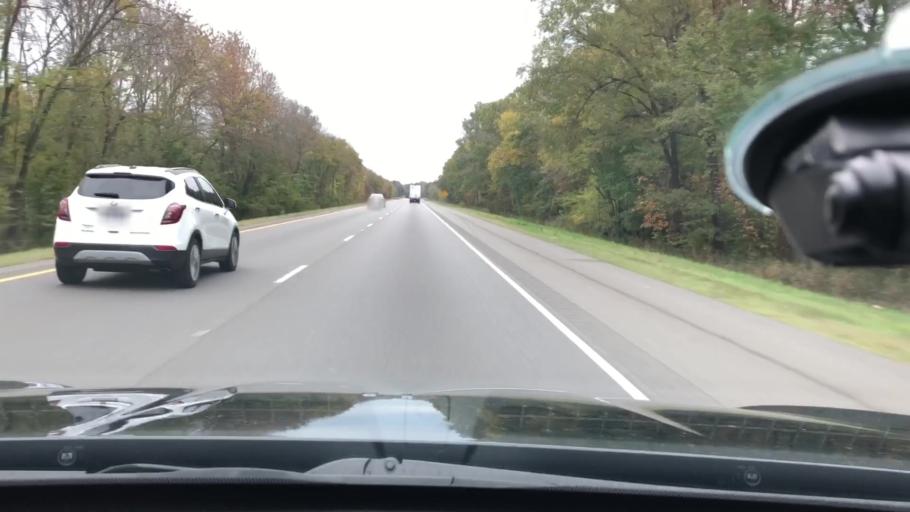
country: US
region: Arkansas
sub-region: Hempstead County
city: Hope
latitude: 33.6555
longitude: -93.6564
